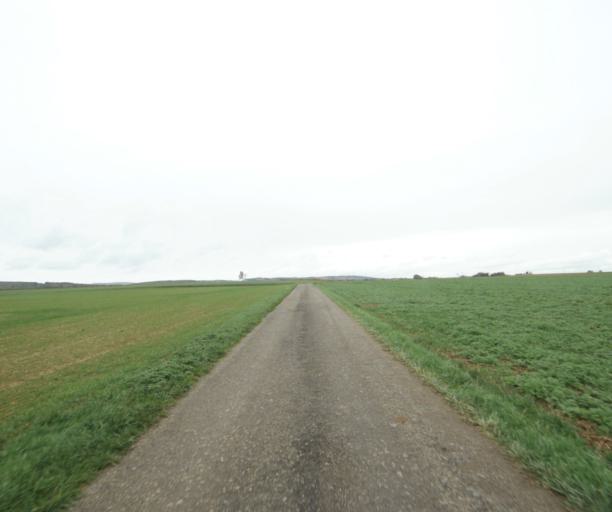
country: FR
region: Bourgogne
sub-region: Departement de Saone-et-Loire
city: Saint-Martin-Belle-Roche
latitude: 46.4644
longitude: 4.8634
